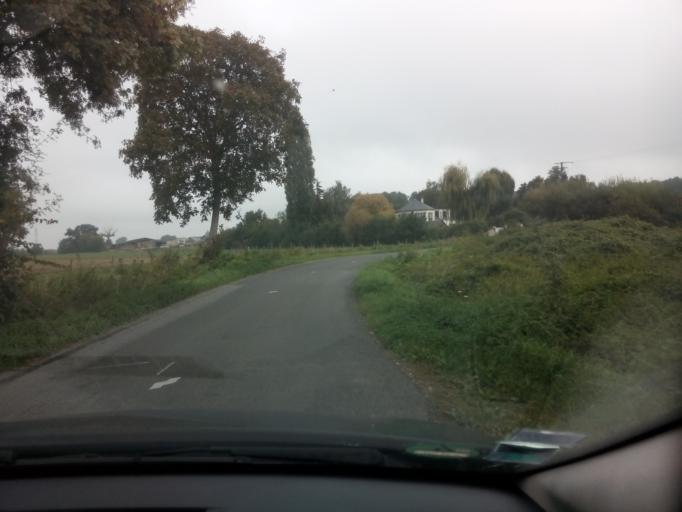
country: FR
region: Pays de la Loire
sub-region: Departement de Maine-et-Loire
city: Soulaire-et-Bourg
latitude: 47.5719
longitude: -0.5604
